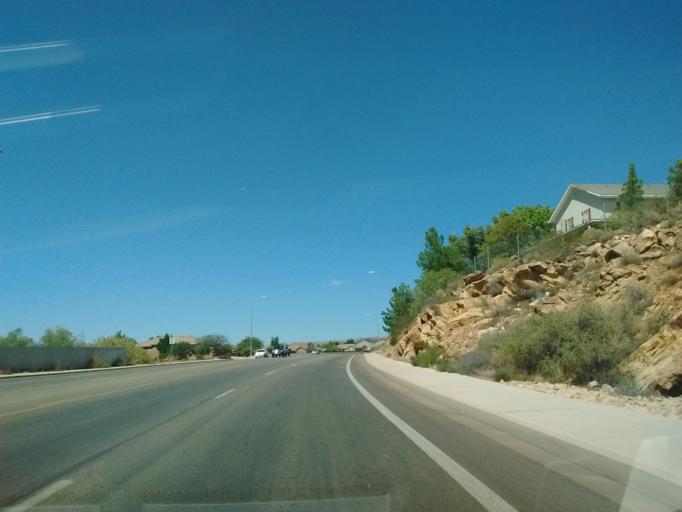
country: US
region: Utah
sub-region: Washington County
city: Washington
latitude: 37.1177
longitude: -113.5032
